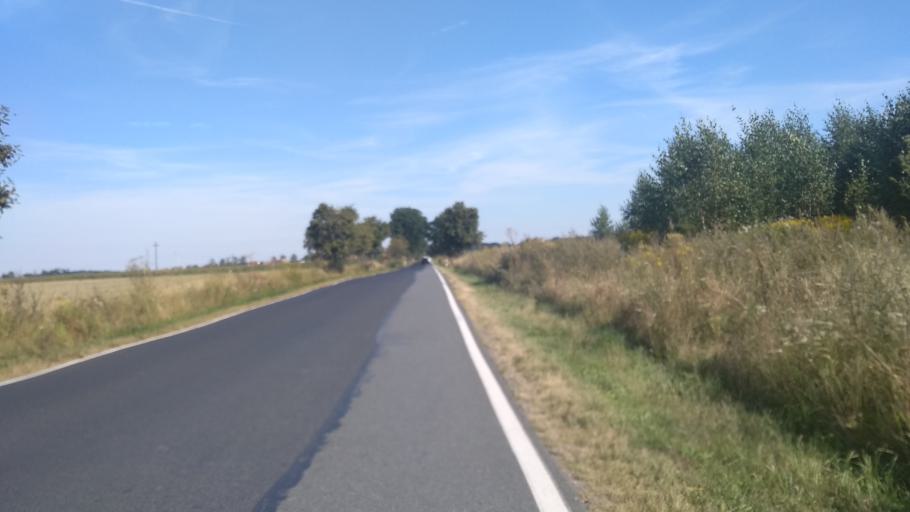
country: PL
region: Kujawsko-Pomorskie
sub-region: Powiat bydgoski
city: Osielsko
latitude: 53.2173
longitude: 18.1403
